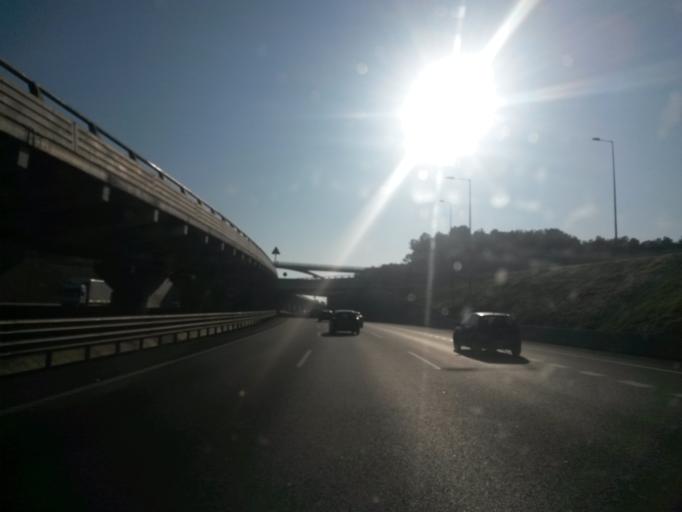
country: ES
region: Catalonia
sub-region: Provincia de Barcelona
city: Ripollet
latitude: 41.4803
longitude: 2.1605
